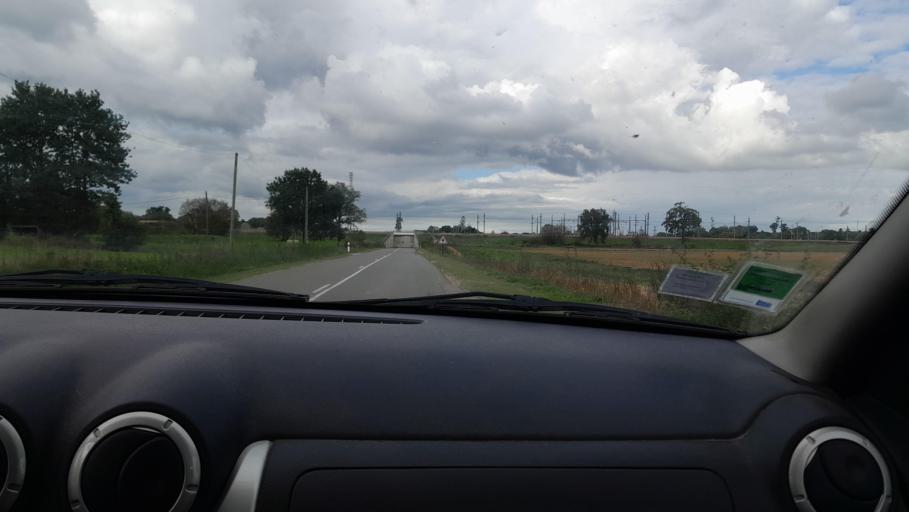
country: FR
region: Brittany
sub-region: Departement d'Ille-et-Vilaine
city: Le Pertre
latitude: 48.0106
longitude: -1.0385
